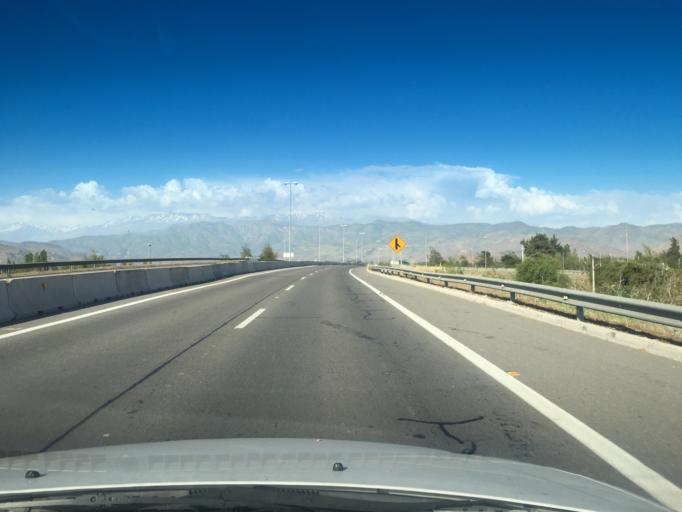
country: CL
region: Santiago Metropolitan
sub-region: Provincia de Chacabuco
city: Chicureo Abajo
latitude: -33.2934
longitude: -70.7035
